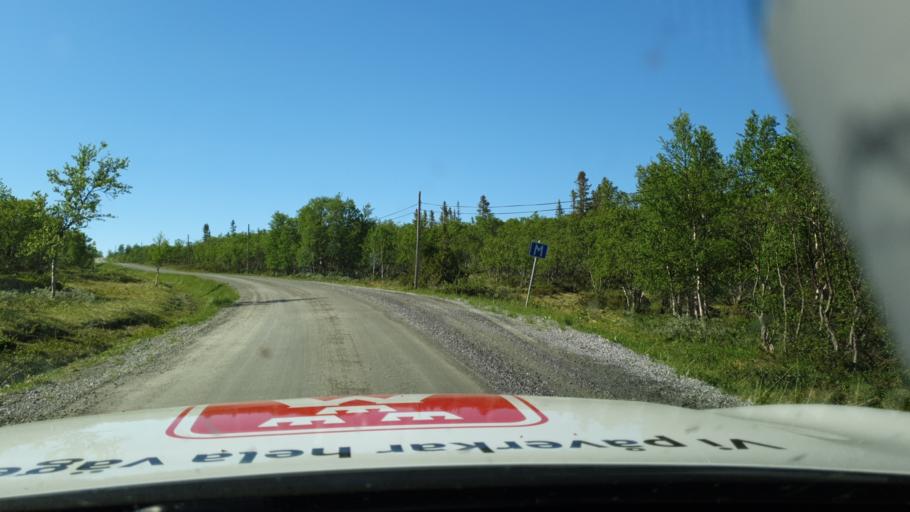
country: SE
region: Jaemtland
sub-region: Are Kommun
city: Are
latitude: 62.8925
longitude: 12.7154
